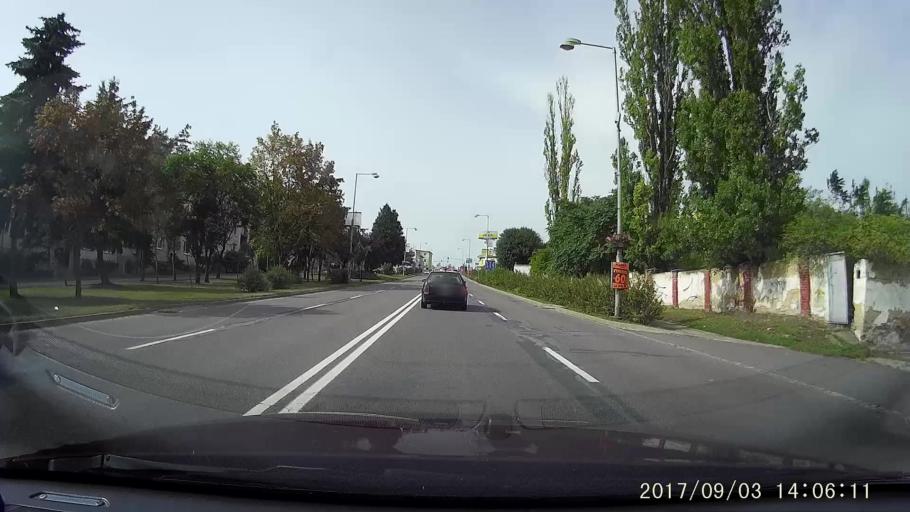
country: CZ
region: South Moravian
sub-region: Okres Znojmo
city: Znojmo
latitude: 48.8442
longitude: 16.0600
